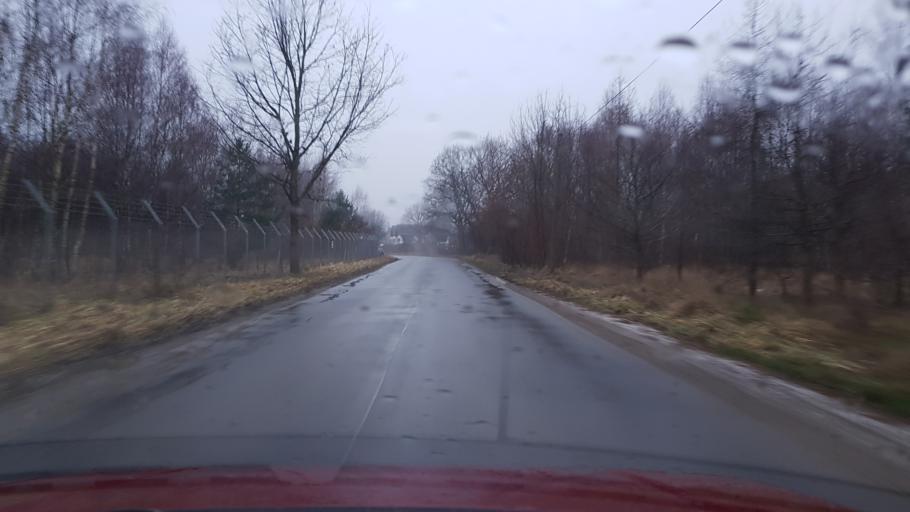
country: PL
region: West Pomeranian Voivodeship
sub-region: Koszalin
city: Koszalin
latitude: 54.1783
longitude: 16.2255
